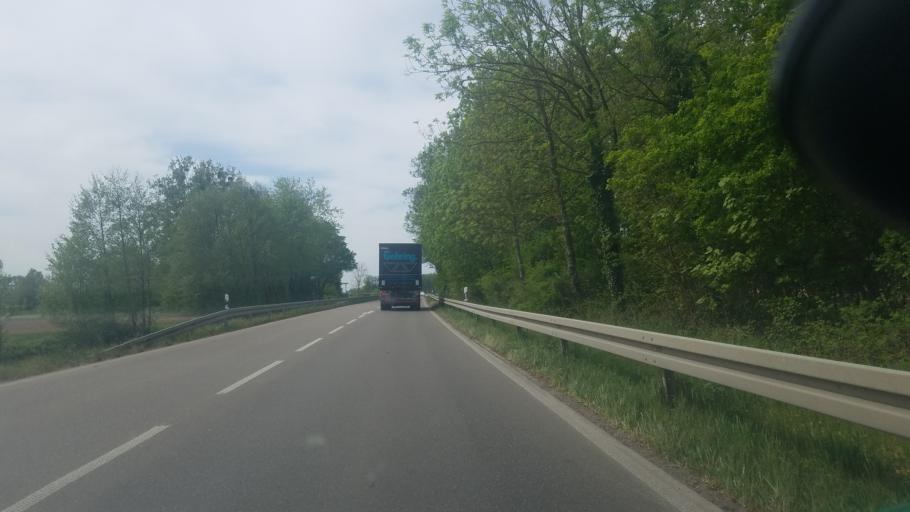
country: DE
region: Baden-Wuerttemberg
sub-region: Freiburg Region
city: Kehl
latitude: 48.5982
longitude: 7.8627
